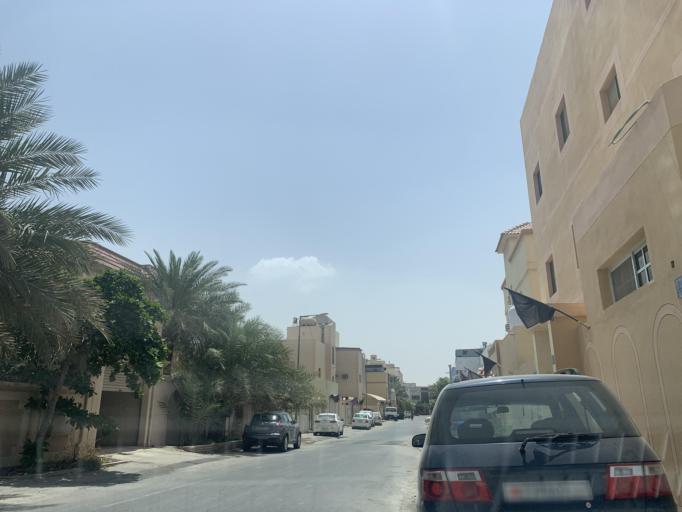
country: BH
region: Central Governorate
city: Madinat Hamad
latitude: 26.1464
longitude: 50.5043
